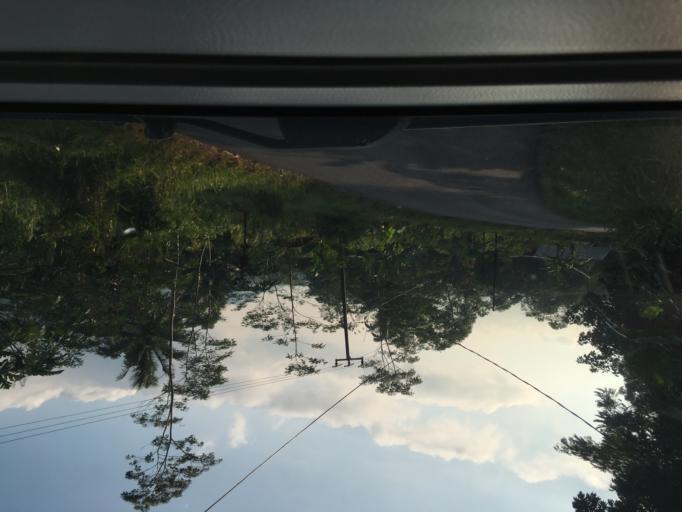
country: ID
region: West Java
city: Maniis
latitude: -7.0365
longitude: 108.3237
